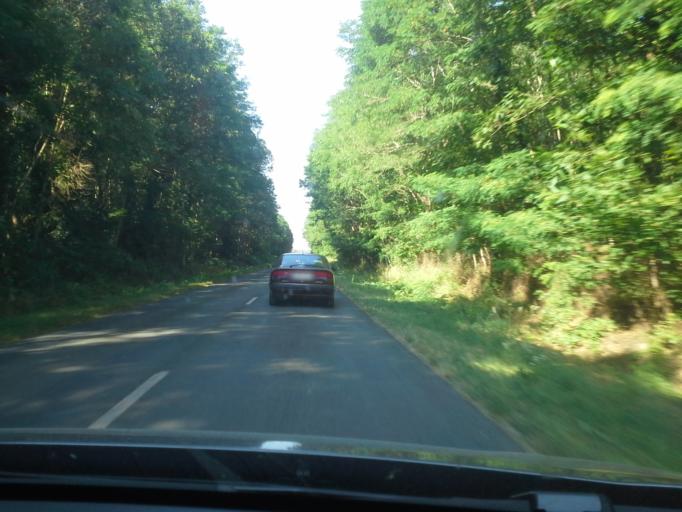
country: FR
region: Centre
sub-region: Departement du Loir-et-Cher
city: Cande-sur-Beuvron
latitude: 47.5013
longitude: 1.2723
